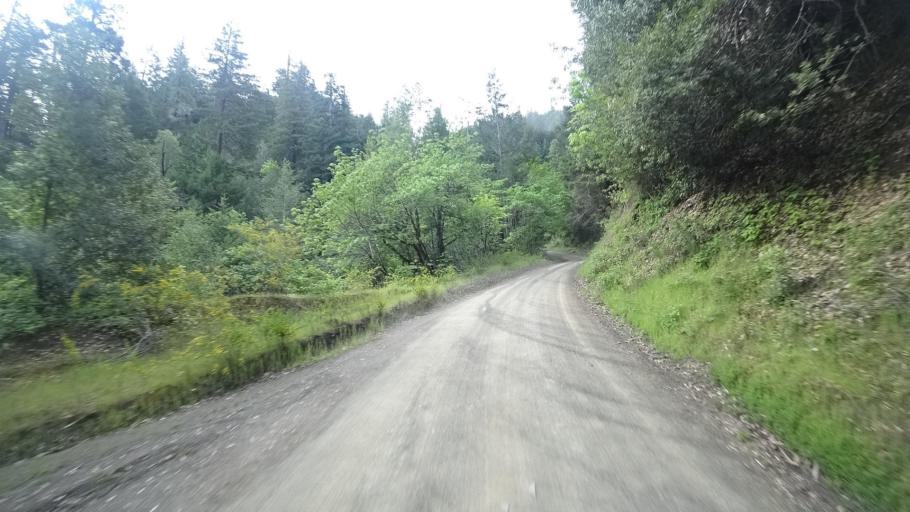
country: US
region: California
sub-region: Humboldt County
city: Redway
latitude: 40.3215
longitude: -123.8347
